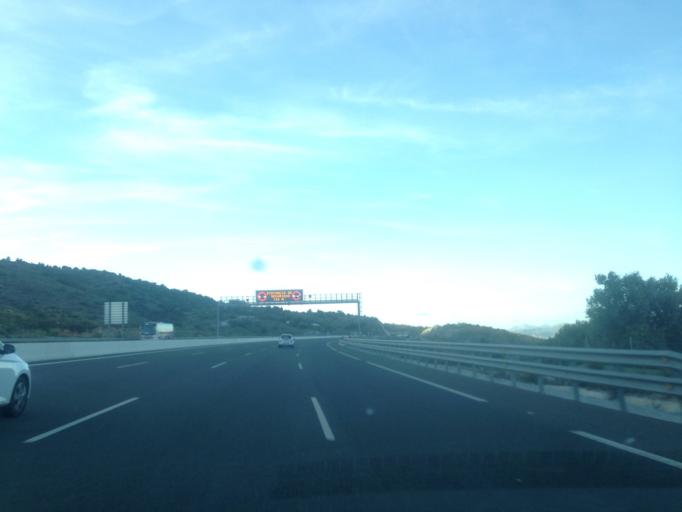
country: ES
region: Andalusia
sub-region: Provincia de Malaga
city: Torremolinos
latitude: 36.6380
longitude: -4.5141
